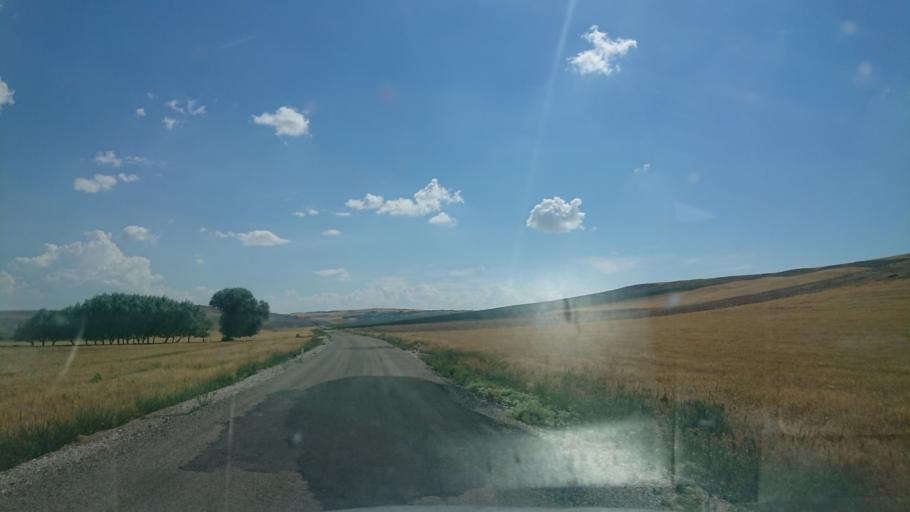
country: TR
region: Aksaray
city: Agacoren
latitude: 38.7939
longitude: 33.8173
